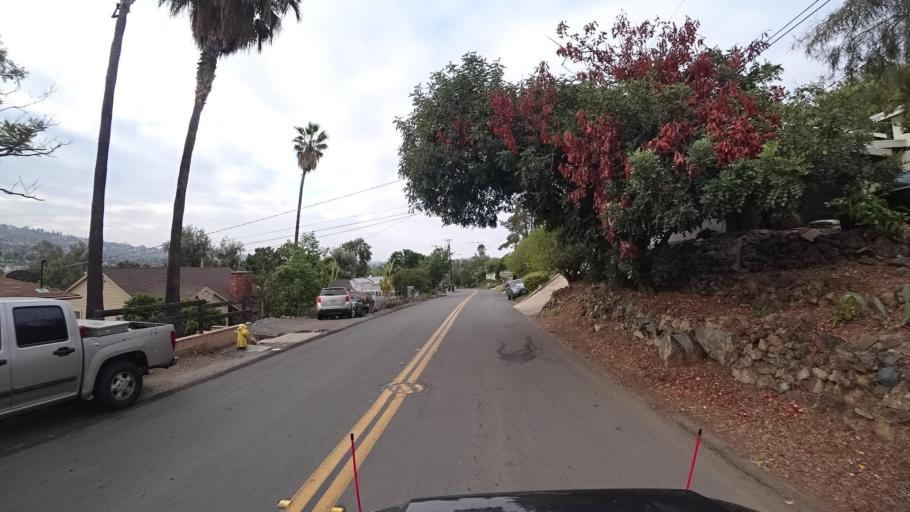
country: US
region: California
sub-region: San Diego County
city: Spring Valley
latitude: 32.7432
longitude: -117.0072
